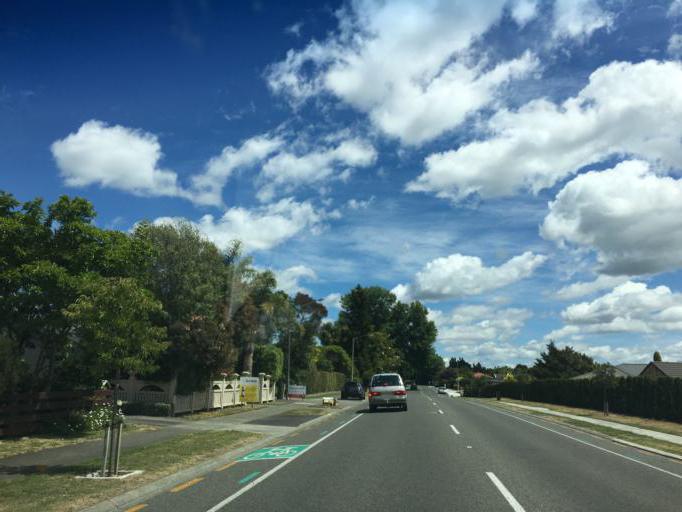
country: NZ
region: Hawke's Bay
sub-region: Hastings District
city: Hastings
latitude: -39.6507
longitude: 176.8660
